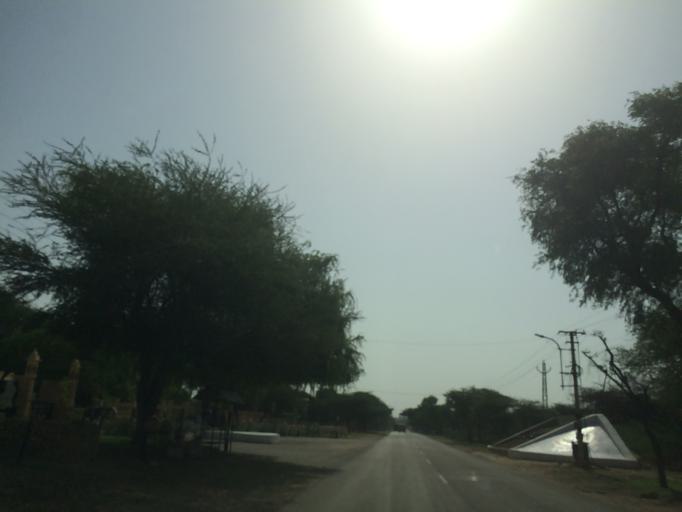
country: IN
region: Rajasthan
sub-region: Jaisalmer
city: Jaisalmer
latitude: 26.9156
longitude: 70.8926
